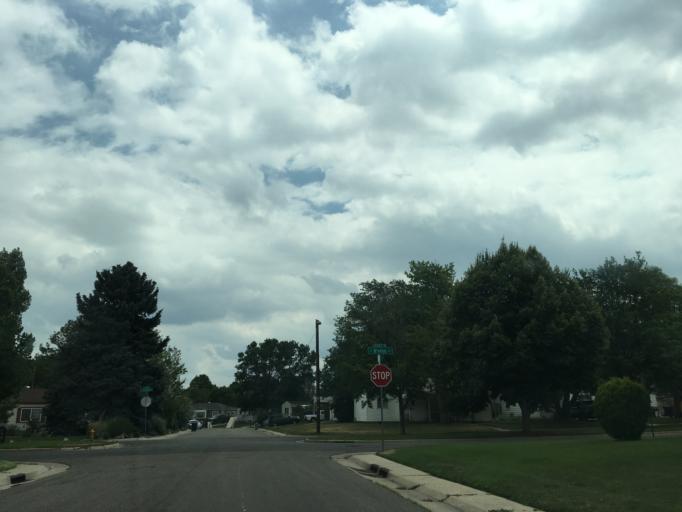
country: US
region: Colorado
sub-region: Arapahoe County
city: Sheridan
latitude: 39.6790
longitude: -105.0302
